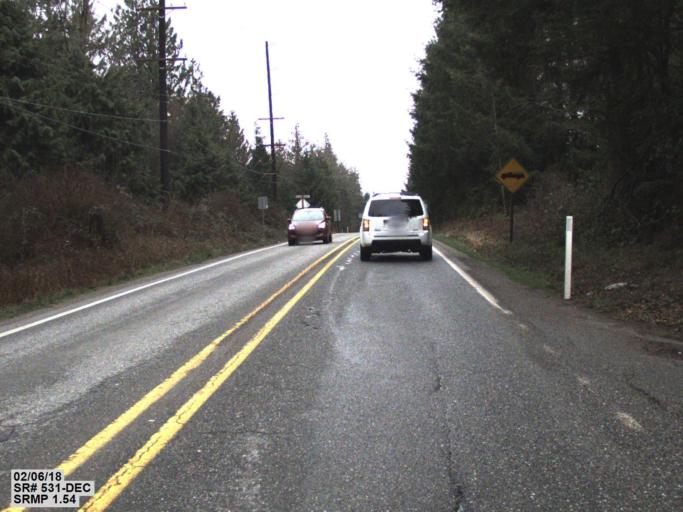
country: US
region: Washington
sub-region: Snohomish County
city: Warm Beach
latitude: 48.1557
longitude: -122.2869
